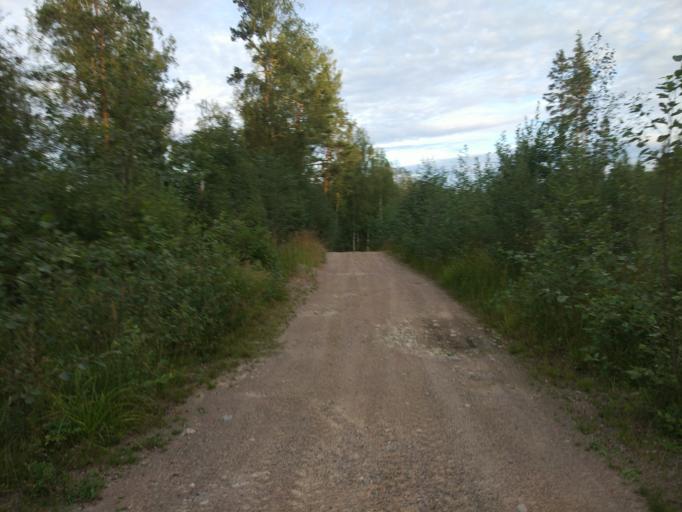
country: RU
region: Leningrad
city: Kuznechnoye
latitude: 61.1155
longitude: 29.6059
